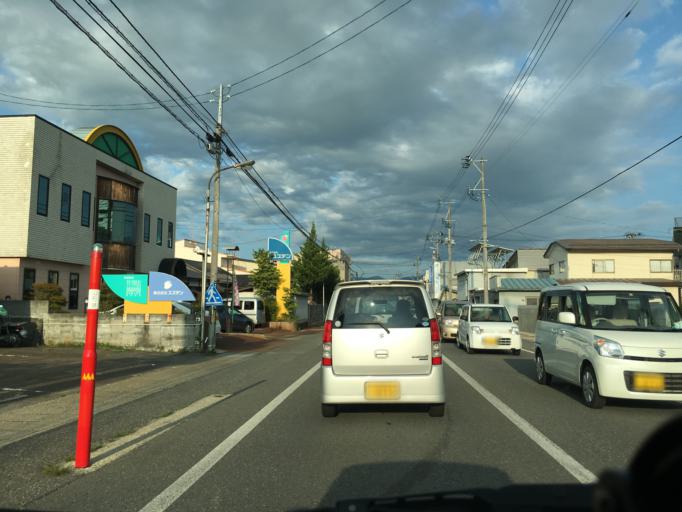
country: JP
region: Yamagata
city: Yonezawa
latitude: 37.9118
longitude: 140.0969
